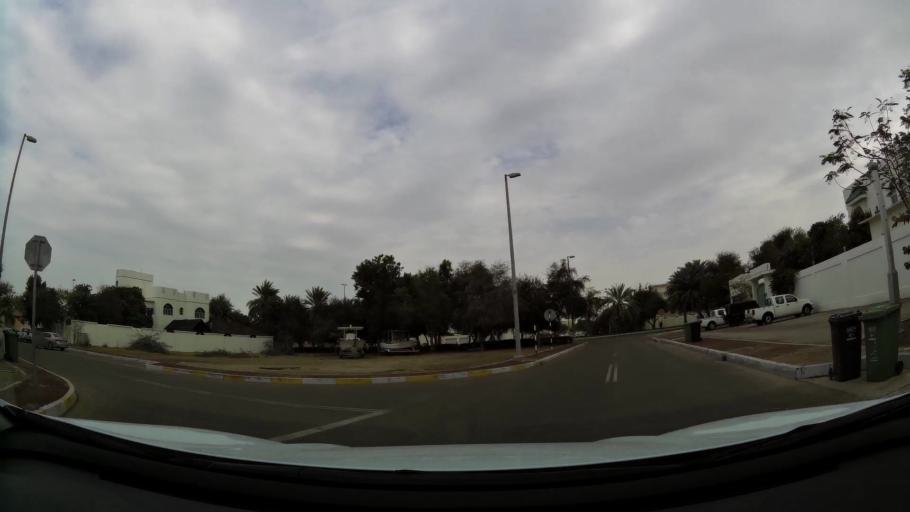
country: AE
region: Abu Dhabi
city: Abu Dhabi
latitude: 24.4301
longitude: 54.4117
